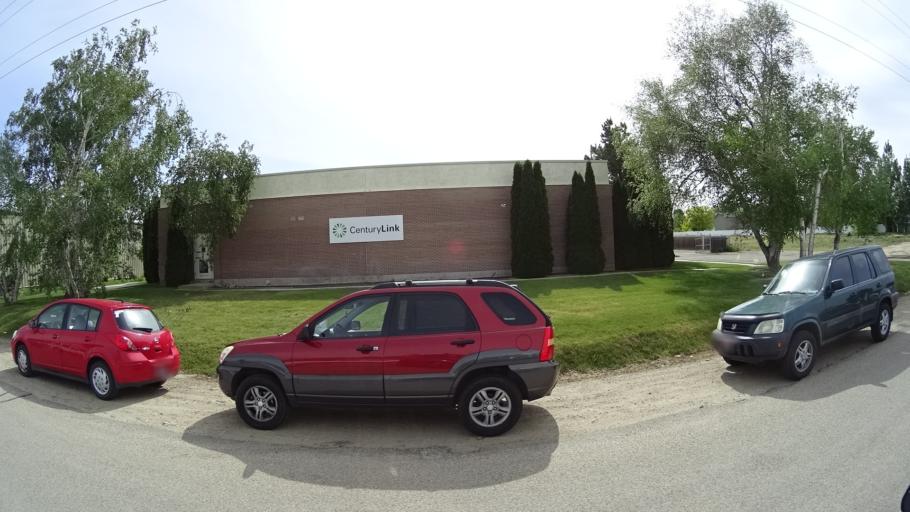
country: US
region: Idaho
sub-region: Ada County
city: Garden City
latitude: 43.5437
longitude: -116.2943
